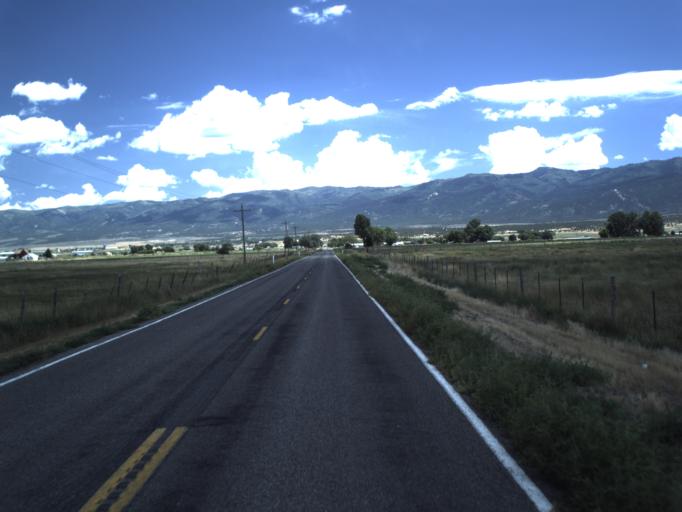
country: US
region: Utah
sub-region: Sanpete County
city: Moroni
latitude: 39.4758
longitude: -111.5845
